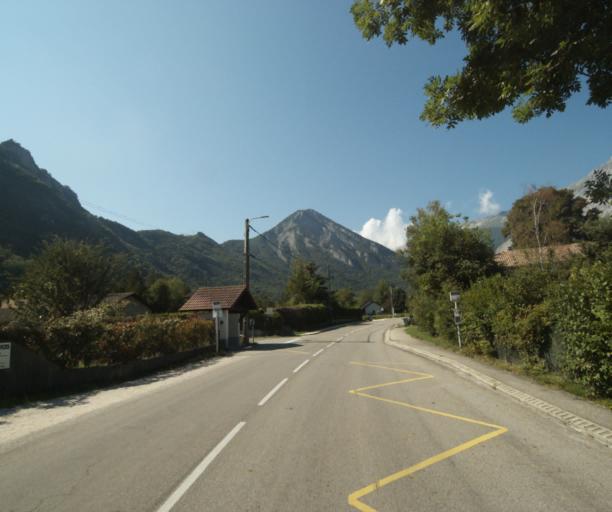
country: FR
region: Rhone-Alpes
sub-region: Departement de l'Isere
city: Saint-Paul-de-Varces
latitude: 45.0745
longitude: 5.6601
